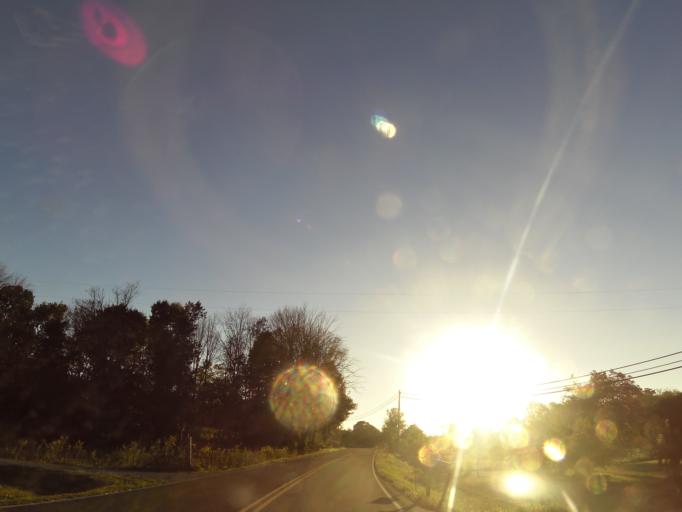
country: US
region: Tennessee
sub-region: Grainger County
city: Rutledge
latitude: 36.3084
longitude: -83.5575
